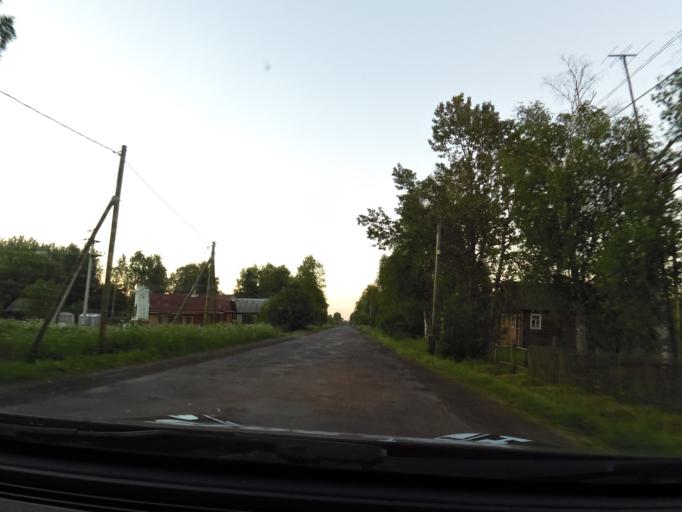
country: RU
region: Leningrad
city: Voznesen'ye
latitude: 60.8271
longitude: 35.7362
